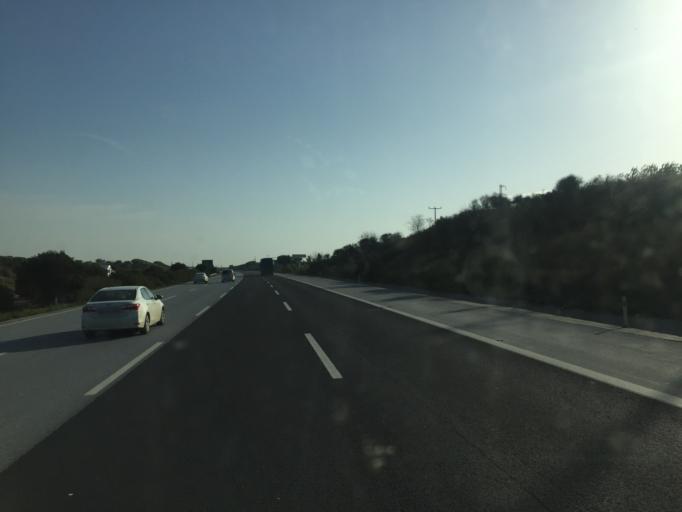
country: TR
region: Mersin
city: Yenice
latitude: 37.0226
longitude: 35.0909
